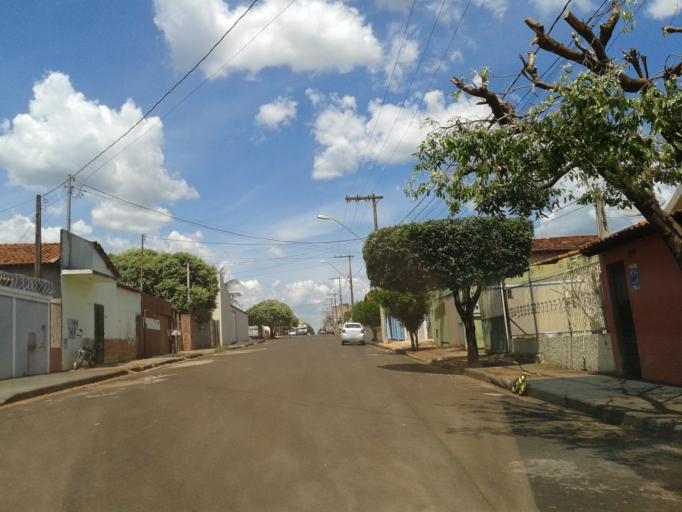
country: BR
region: Minas Gerais
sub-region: Ituiutaba
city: Ituiutaba
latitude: -18.9836
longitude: -49.4709
